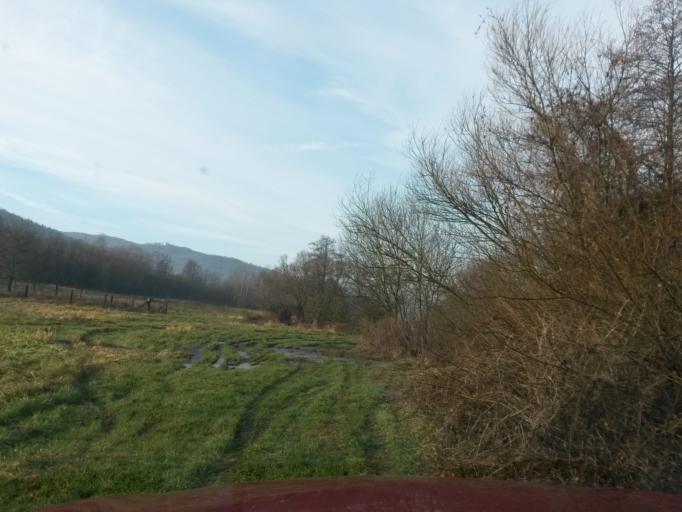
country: SK
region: Kosicky
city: Roznava
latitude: 48.7121
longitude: 20.4521
